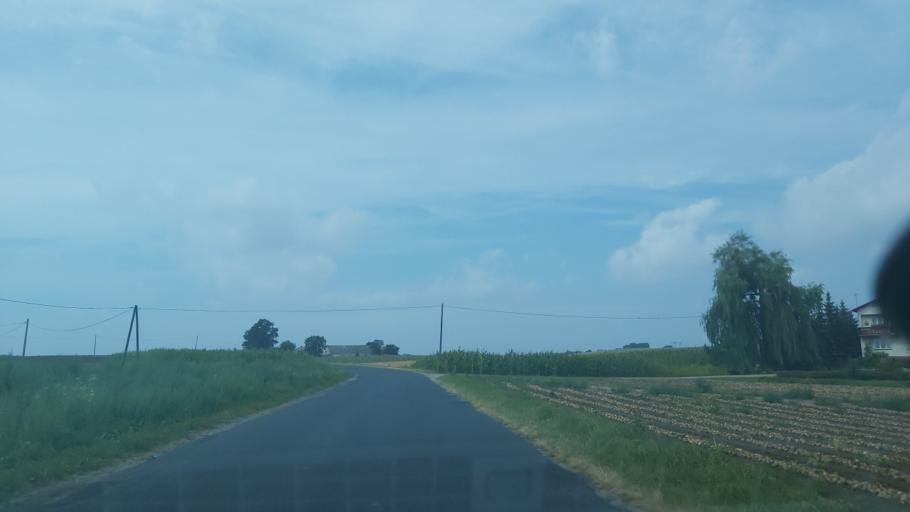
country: PL
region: Kujawsko-Pomorskie
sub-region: Powiat golubsko-dobrzynski
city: Zbojno
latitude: 53.0480
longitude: 19.1600
